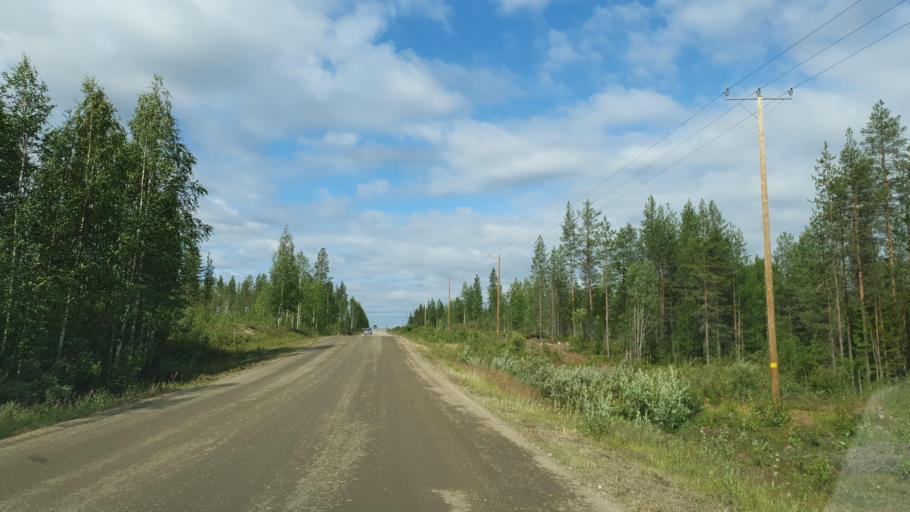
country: FI
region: Lapland
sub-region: Pohjois-Lappi
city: Sodankylae
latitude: 67.5363
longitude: 25.9664
